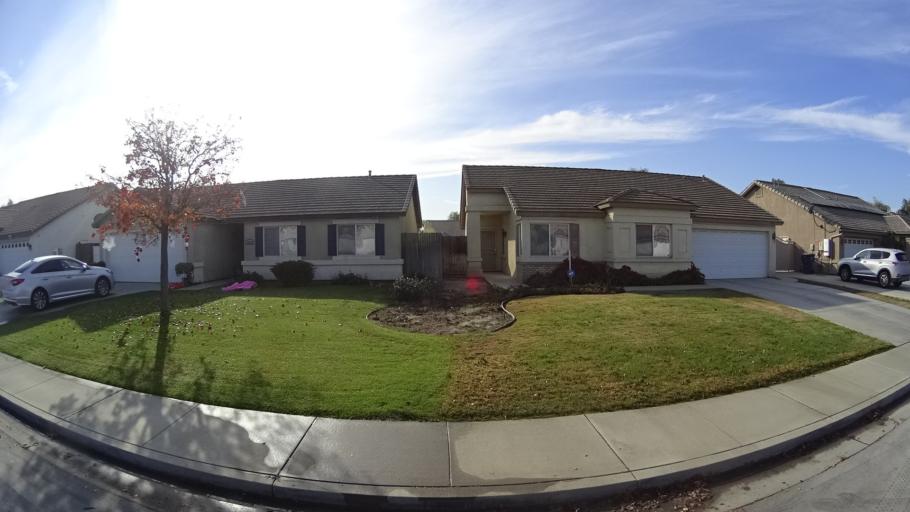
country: US
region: California
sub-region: Kern County
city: Rosedale
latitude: 35.4046
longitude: -119.1399
